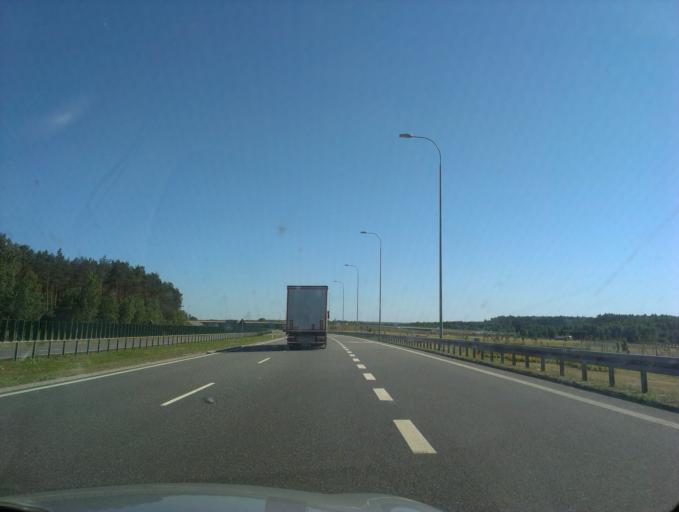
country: PL
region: Kujawsko-Pomorskie
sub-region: Powiat swiecki
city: Warlubie
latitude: 53.4699
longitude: 18.6180
